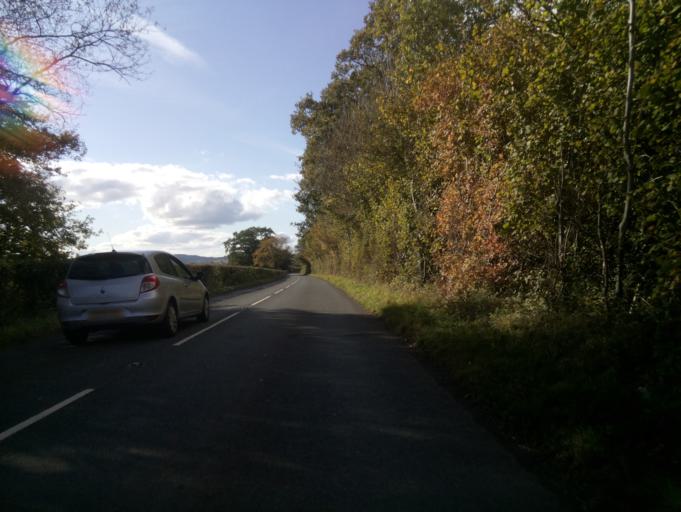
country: GB
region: Wales
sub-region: Sir Powys
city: Brecon
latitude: 51.9605
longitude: -3.3692
